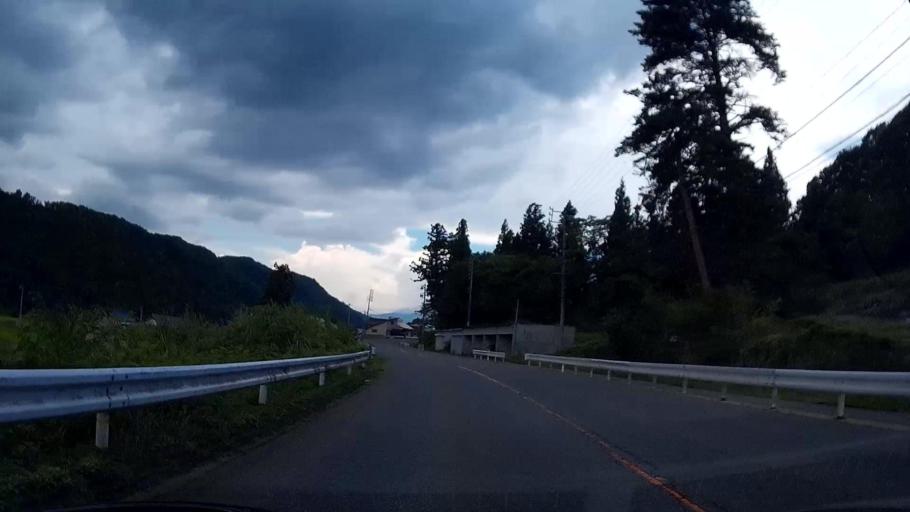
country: JP
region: Nagano
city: Iiyama
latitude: 36.9856
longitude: 138.5286
